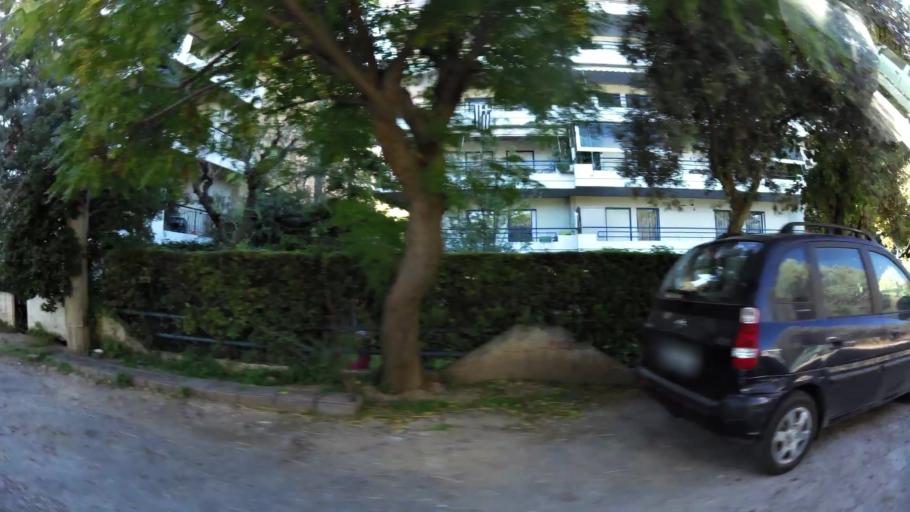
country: GR
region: Attica
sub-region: Nomarchia Athinas
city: Vrilissia
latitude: 38.0352
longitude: 23.8158
